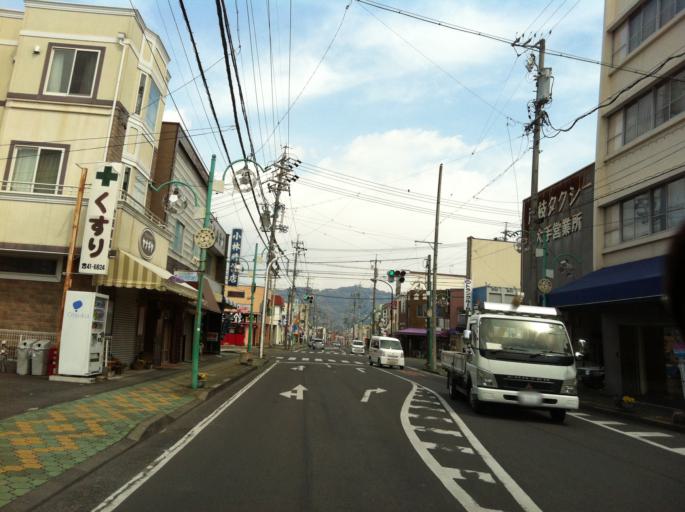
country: JP
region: Shizuoka
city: Fujieda
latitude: 34.8752
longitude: 138.2649
